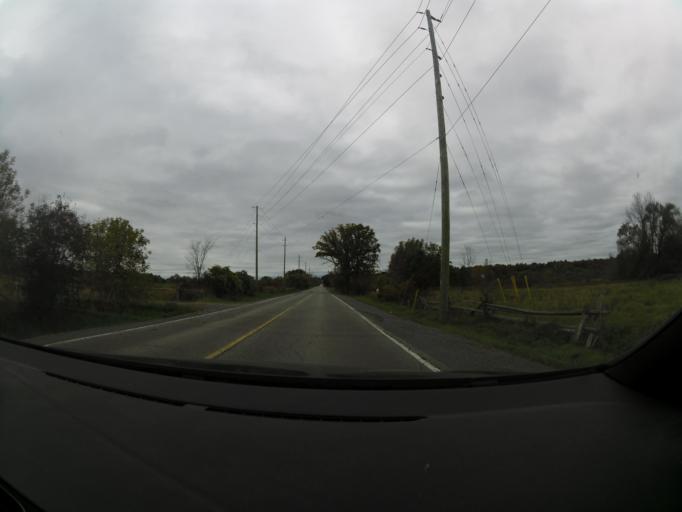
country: CA
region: Ontario
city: Bells Corners
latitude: 45.3194
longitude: -75.9585
